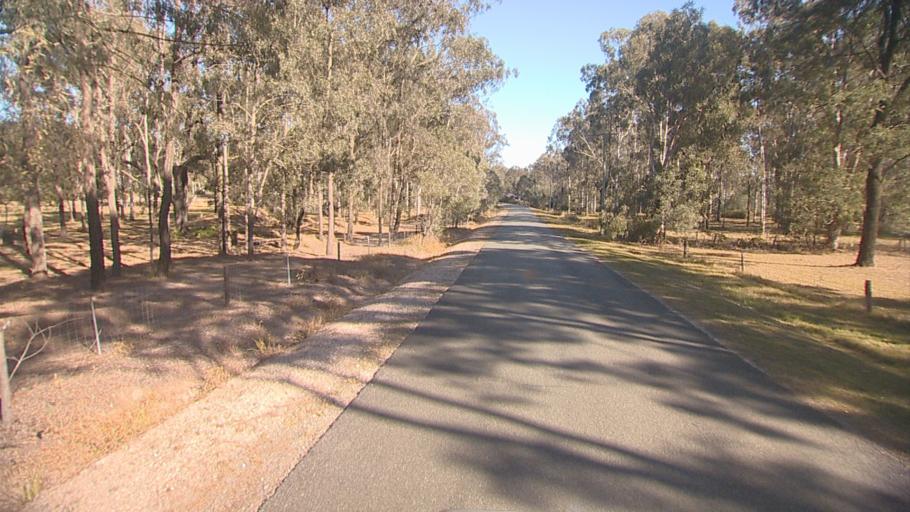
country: AU
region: Queensland
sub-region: Logan
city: Chambers Flat
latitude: -27.7874
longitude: 153.1349
